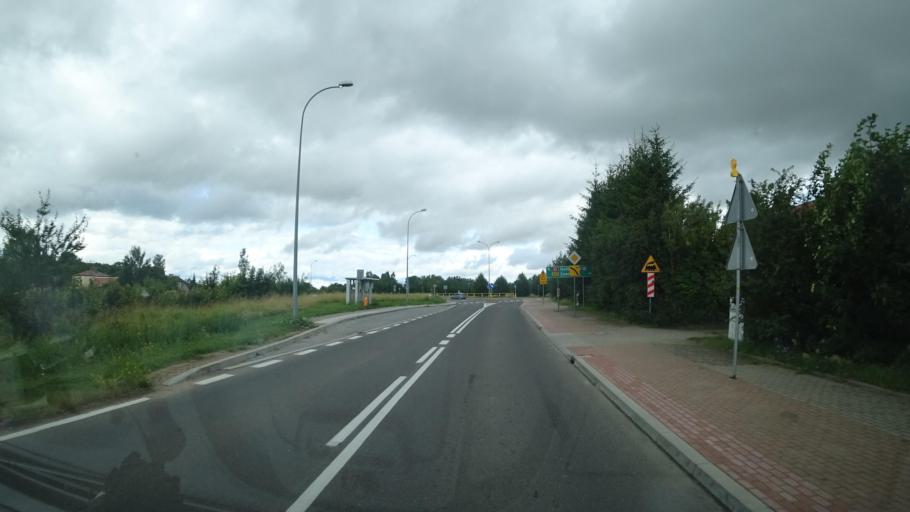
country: PL
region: Warmian-Masurian Voivodeship
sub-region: Powiat olecki
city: Kowale Oleckie
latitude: 54.1739
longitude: 22.4151
